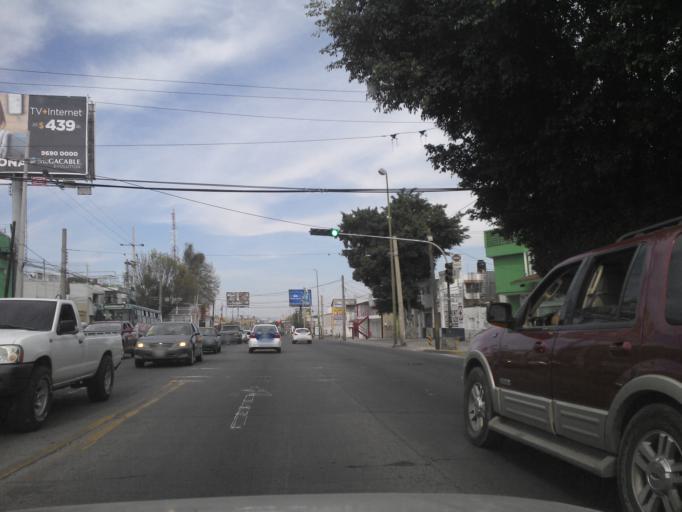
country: MX
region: Jalisco
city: Guadalajara
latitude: 20.6528
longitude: -103.3589
